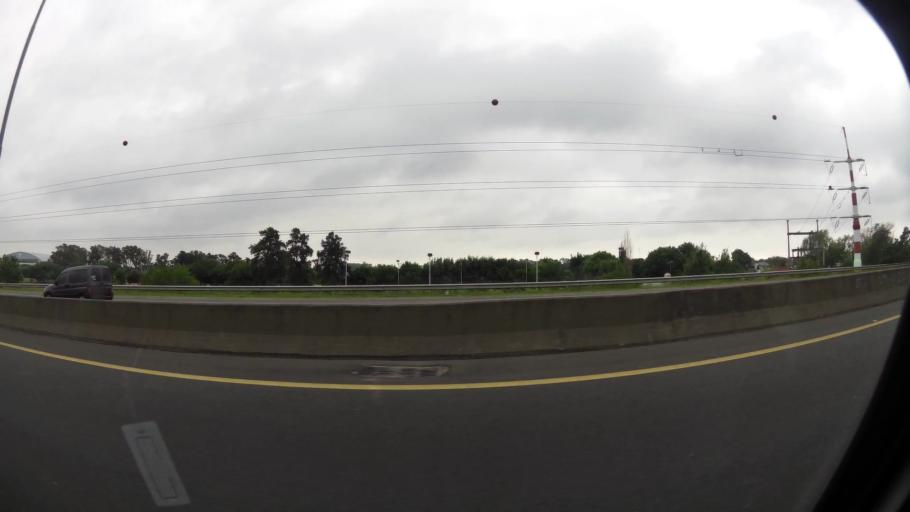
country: AR
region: Buenos Aires
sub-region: Partido de Quilmes
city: Quilmes
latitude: -34.7143
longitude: -58.2448
